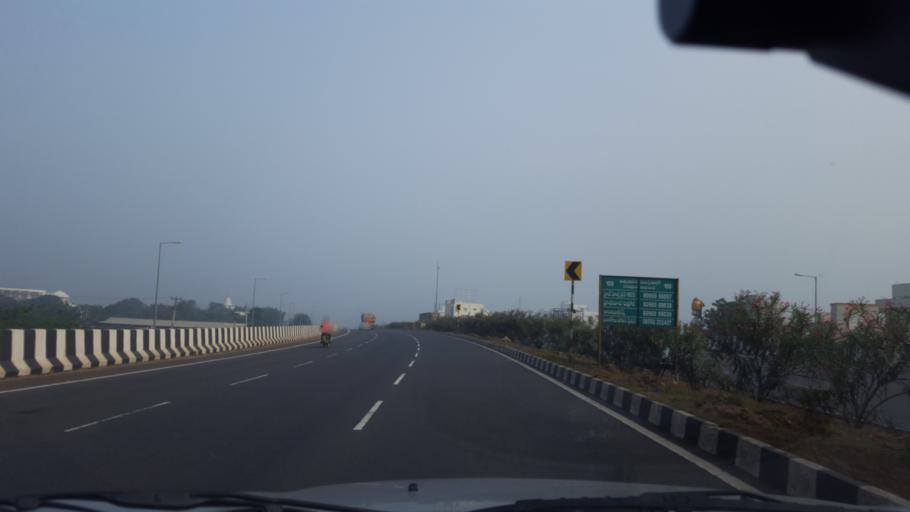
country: IN
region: Andhra Pradesh
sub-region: Prakasam
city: Ongole
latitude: 15.4560
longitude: 80.0477
